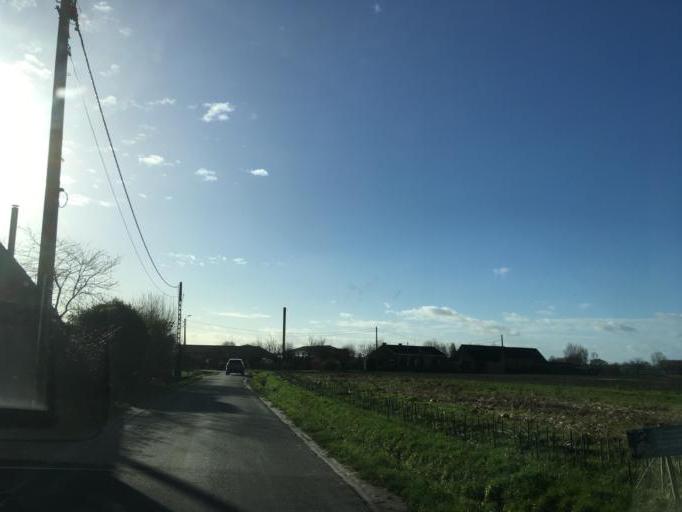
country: BE
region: Flanders
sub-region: Provincie West-Vlaanderen
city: Ardooie
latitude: 50.9845
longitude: 3.1737
